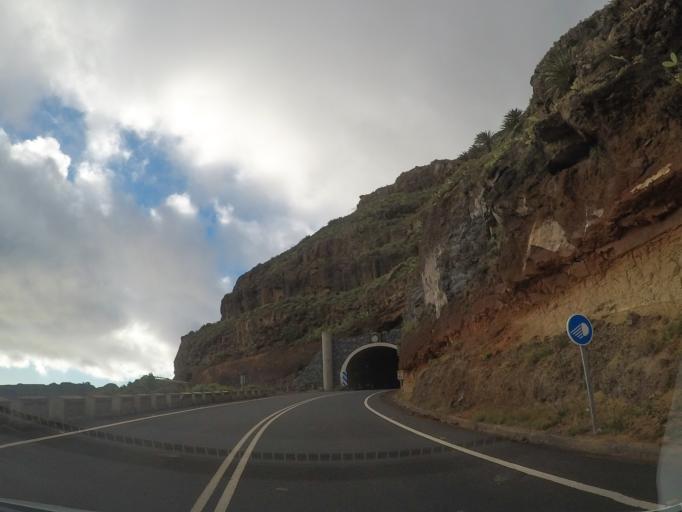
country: ES
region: Canary Islands
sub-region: Provincia de Santa Cruz de Tenerife
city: Vallehermosa
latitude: 28.1222
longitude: -17.3185
